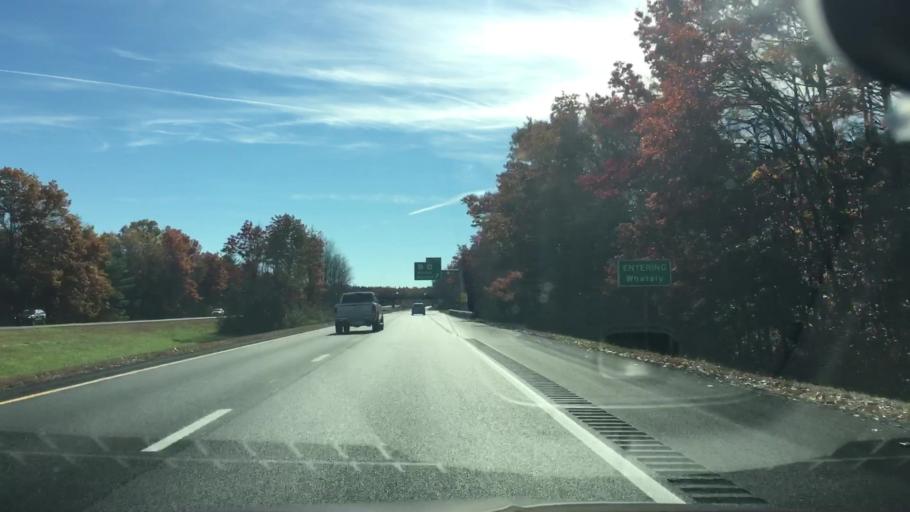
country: US
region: Massachusetts
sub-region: Franklin County
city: South Deerfield
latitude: 42.4708
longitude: -72.6171
